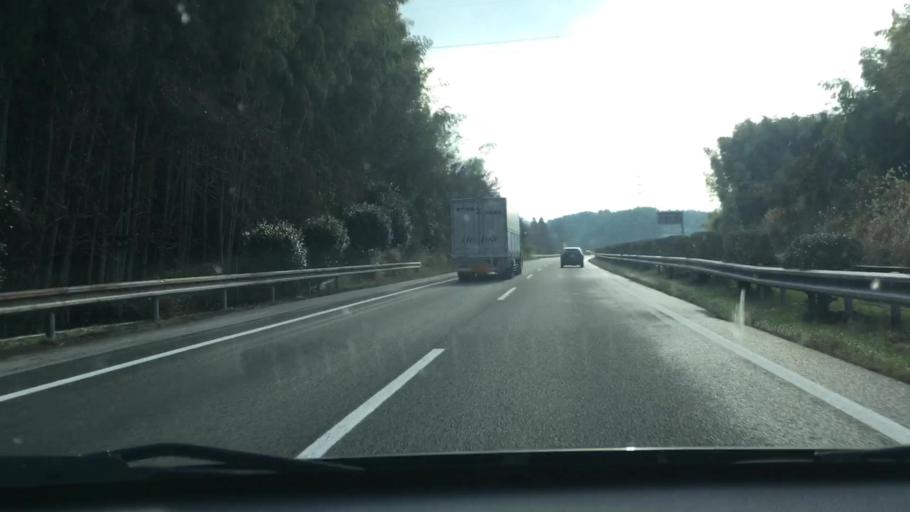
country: JP
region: Kumamoto
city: Uto
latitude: 32.6873
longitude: 130.7360
